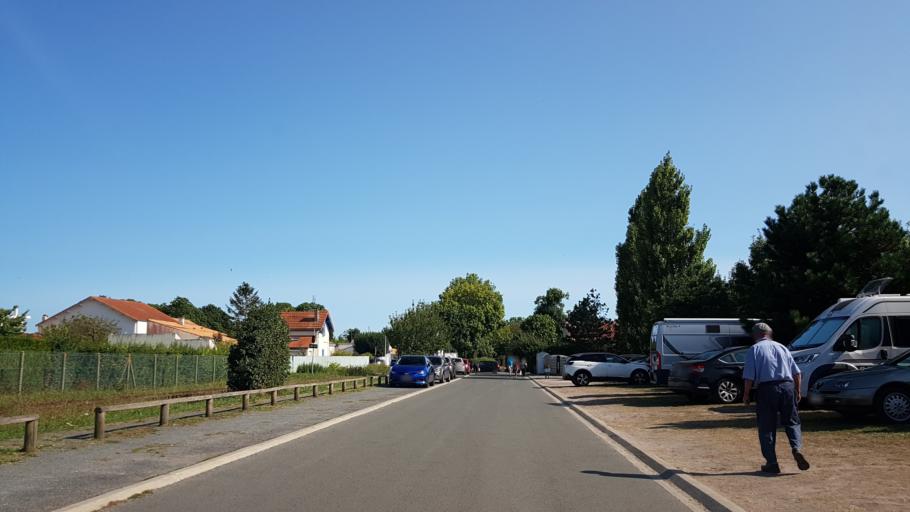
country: FR
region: Poitou-Charentes
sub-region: Departement de la Charente-Maritime
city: Breuillet
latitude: 45.7080
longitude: -1.0313
